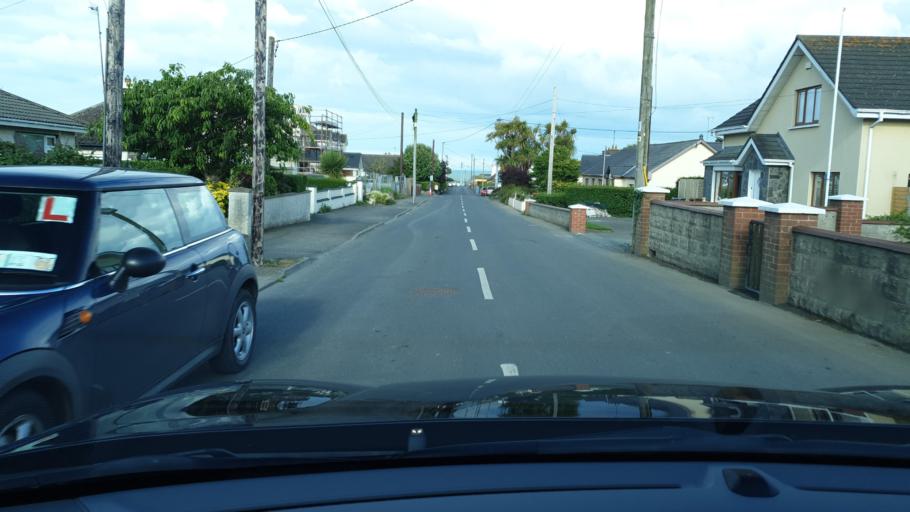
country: IE
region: Leinster
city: An Ros
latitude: 53.5469
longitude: -6.0878
